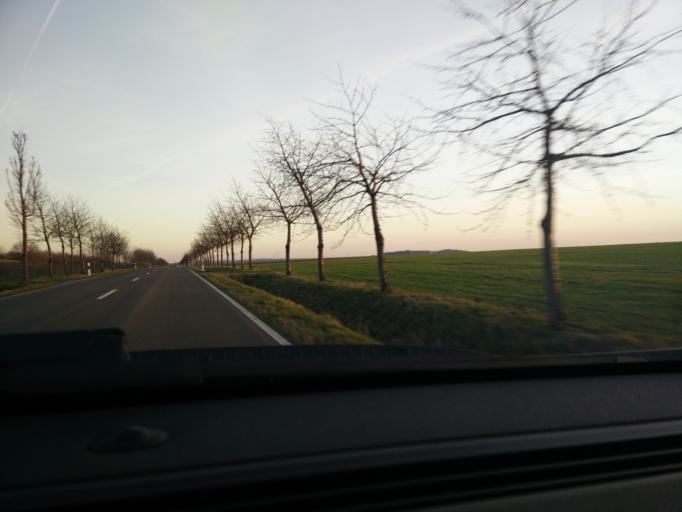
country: DE
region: Saxony
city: Bad Lausick
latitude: 51.1213
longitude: 12.6681
